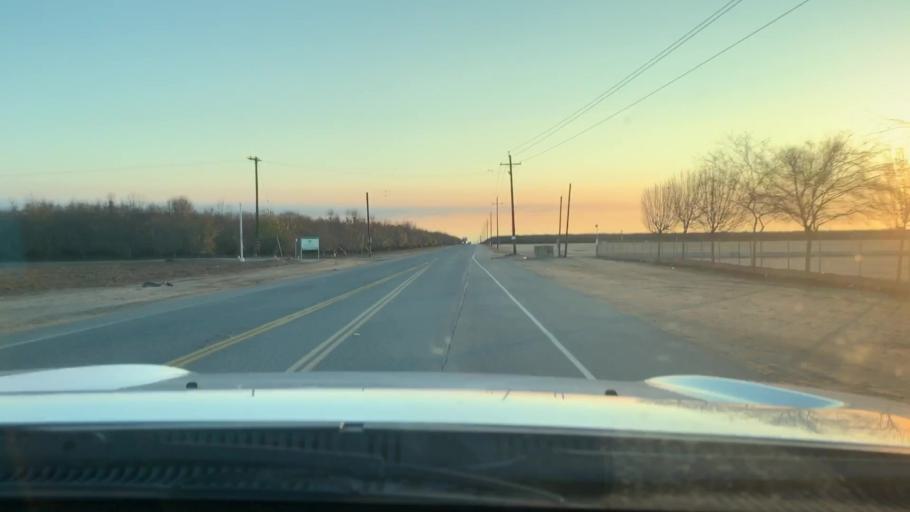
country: US
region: California
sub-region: Kern County
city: Buttonwillow
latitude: 35.5008
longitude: -119.5246
